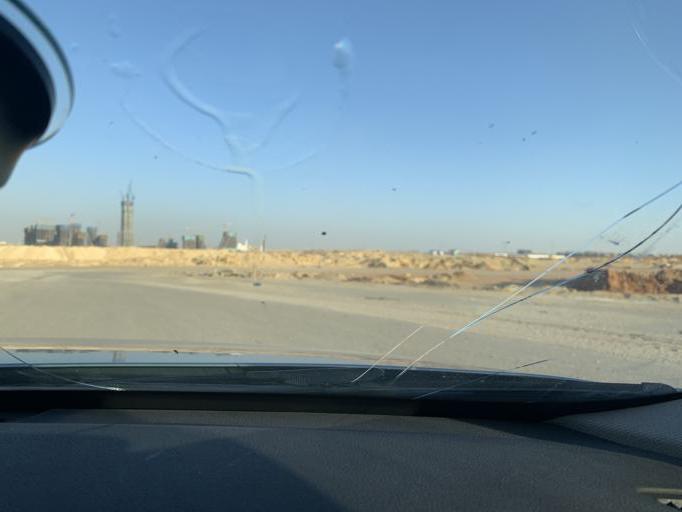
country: EG
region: Muhafazat al Qalyubiyah
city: Al Khankah
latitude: 30.0232
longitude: 31.6772
